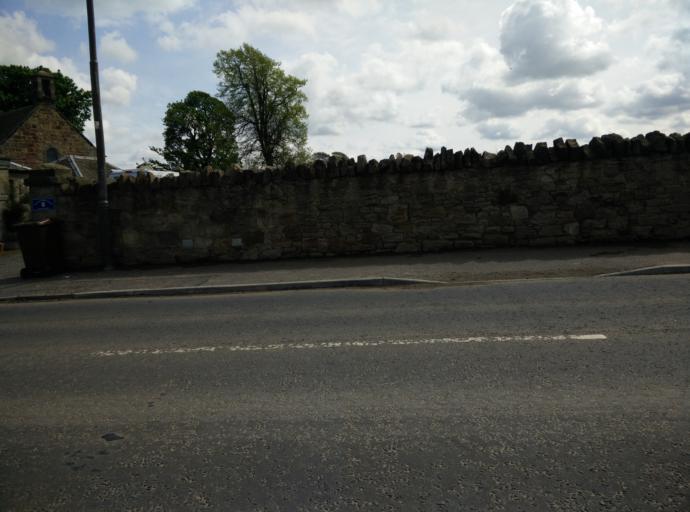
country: GB
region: Scotland
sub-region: Midlothian
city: Dalkeith
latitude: 55.9123
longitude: -3.0985
